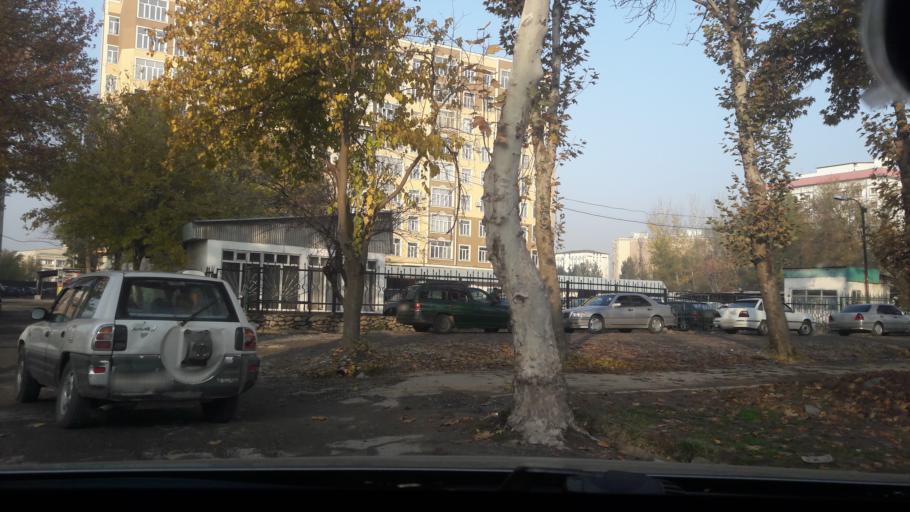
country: TJ
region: Dushanbe
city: Dushanbe
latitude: 38.5811
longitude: 68.7550
